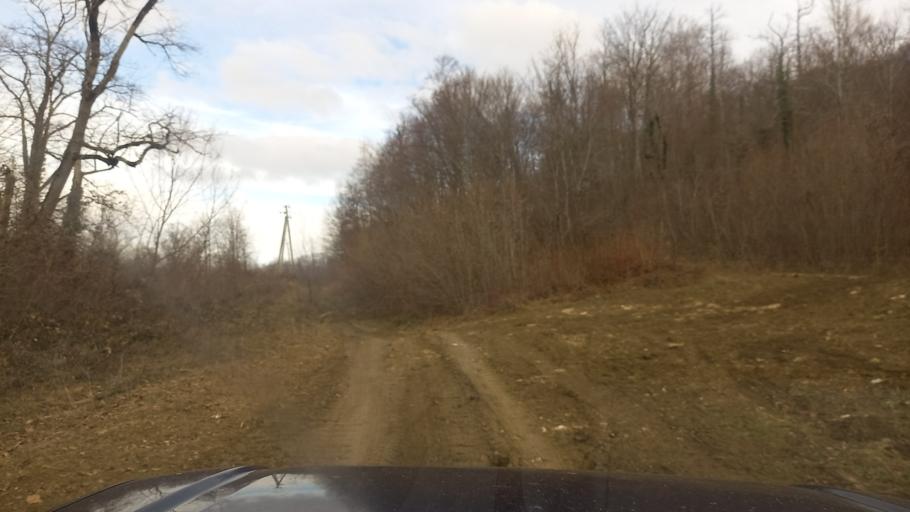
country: RU
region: Krasnodarskiy
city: Neftegorsk
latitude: 44.2026
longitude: 39.7039
